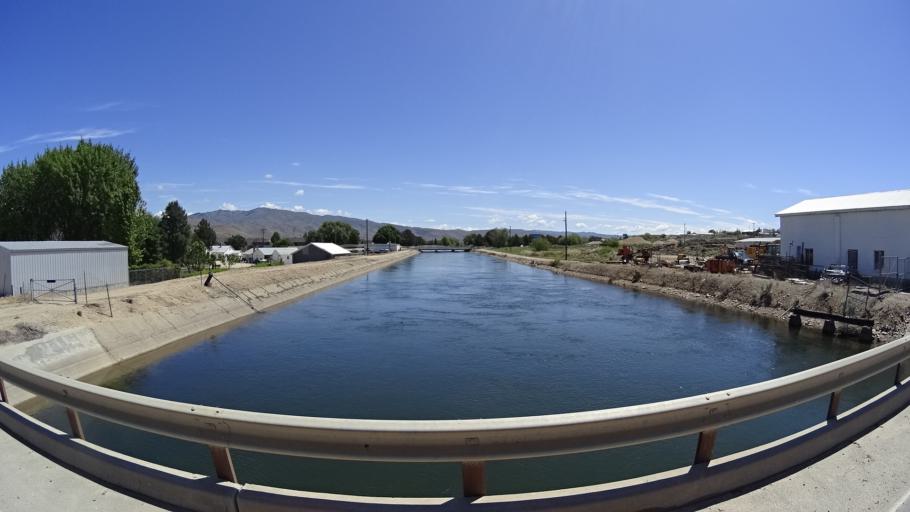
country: US
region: Idaho
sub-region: Ada County
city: Boise
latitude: 43.5667
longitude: -116.1835
